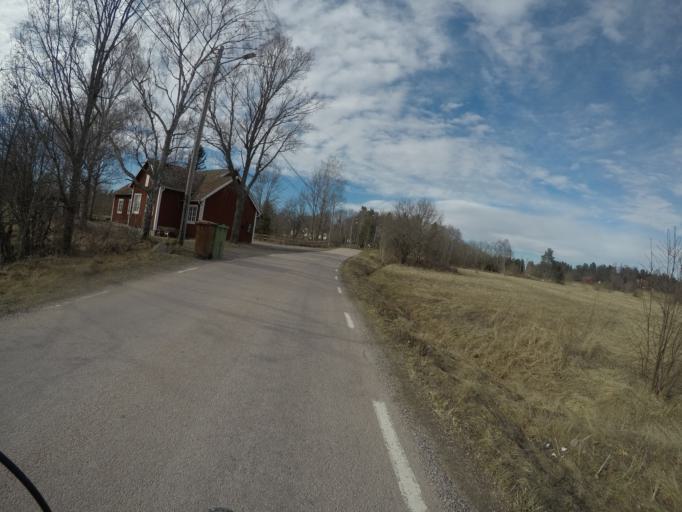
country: SE
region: Vaestmanland
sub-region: Kungsors Kommun
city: Kungsoer
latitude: 59.4201
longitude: 16.1889
